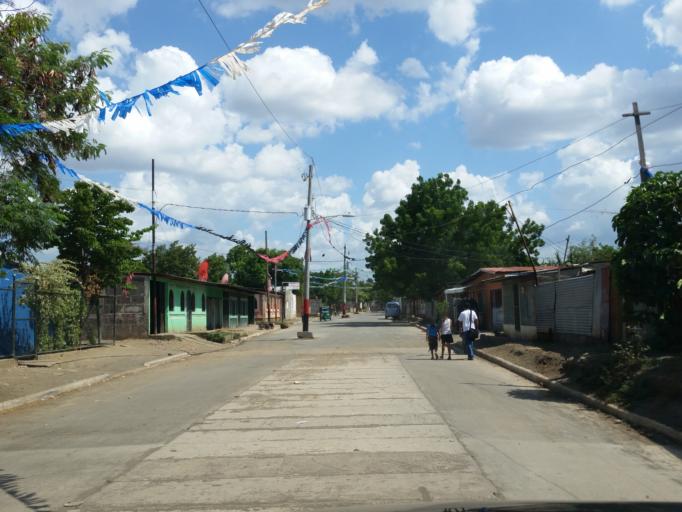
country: NI
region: Managua
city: Managua
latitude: 12.1594
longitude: -86.2029
